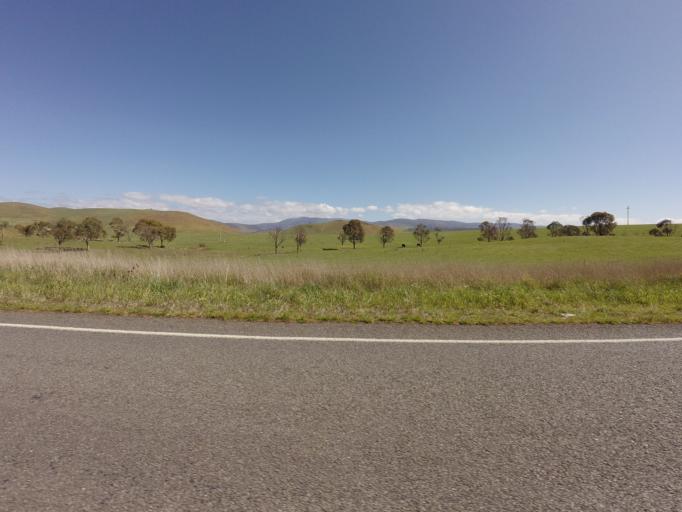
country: AU
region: Tasmania
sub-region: Derwent Valley
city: New Norfolk
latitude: -42.5417
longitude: 146.7731
